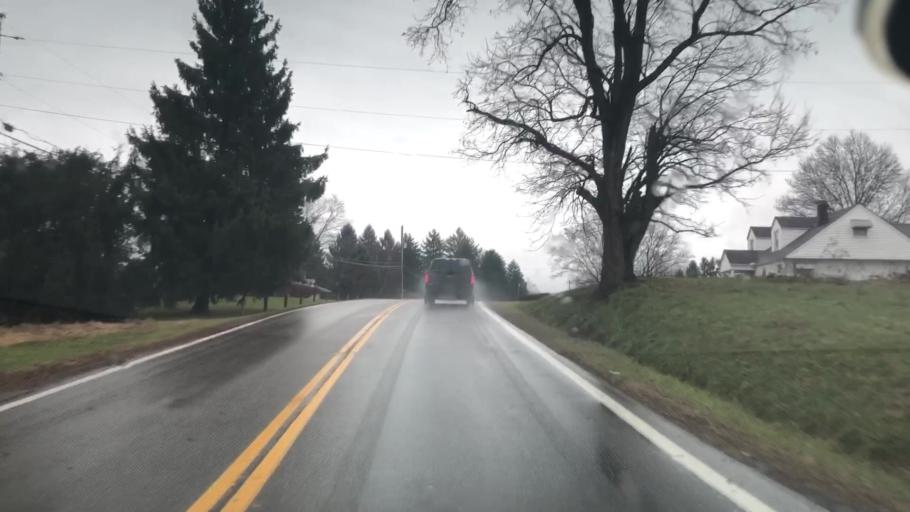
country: US
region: Ohio
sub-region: Belmont County
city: Saint Clairsville
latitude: 40.1065
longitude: -80.9284
